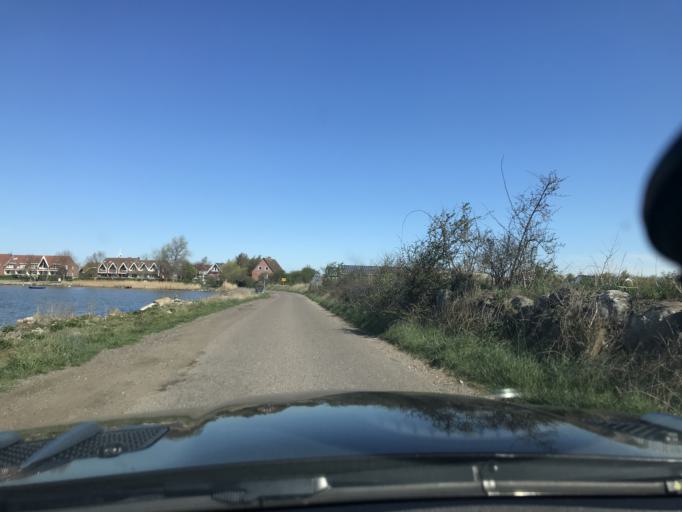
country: DE
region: Schleswig-Holstein
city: Grossenbrode
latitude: 54.4449
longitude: 11.0959
